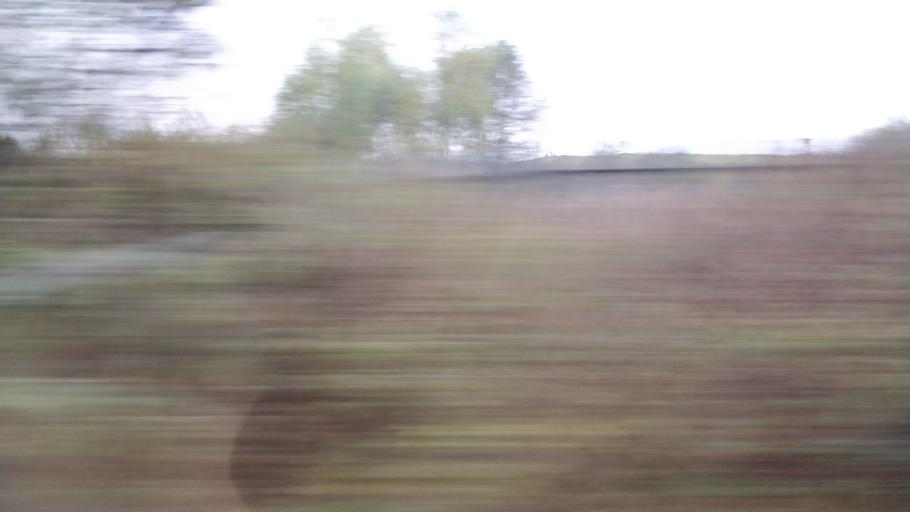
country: GB
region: England
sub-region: Borough of Wigan
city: Tyldesley
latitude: 53.5282
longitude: -2.4655
